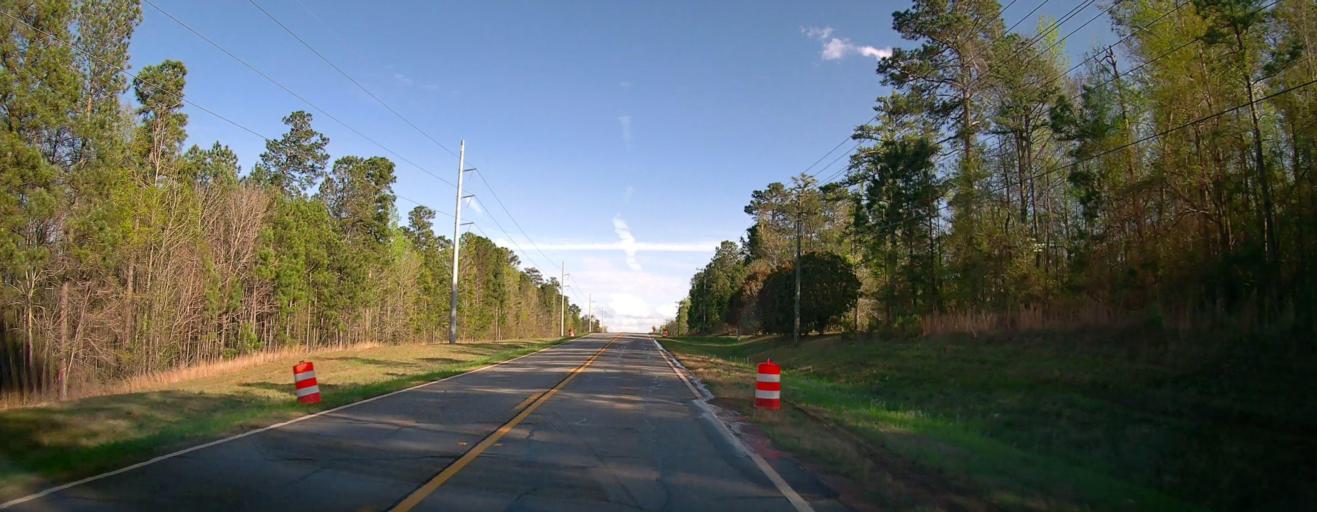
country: US
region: Georgia
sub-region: Baldwin County
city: Milledgeville
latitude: 33.1390
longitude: -83.3295
